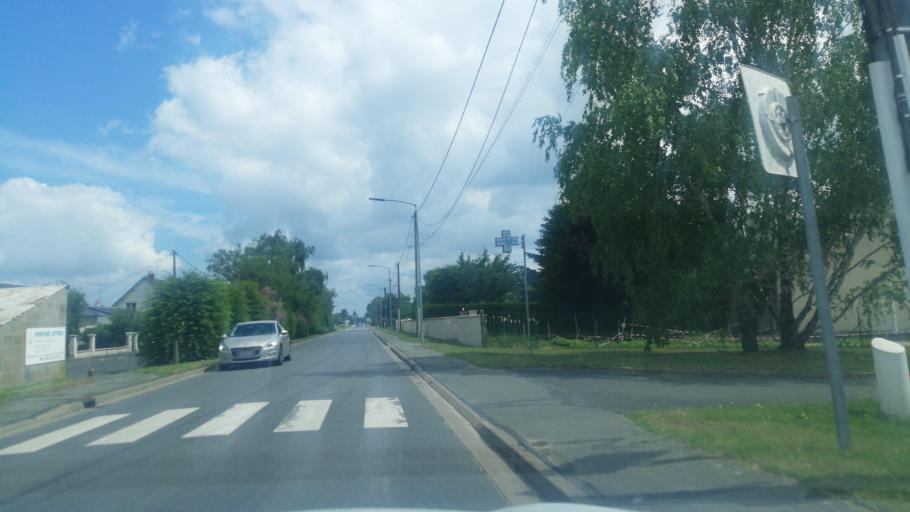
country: FR
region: Centre
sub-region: Departement du Loir-et-Cher
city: Contres
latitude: 47.4256
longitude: 1.4310
